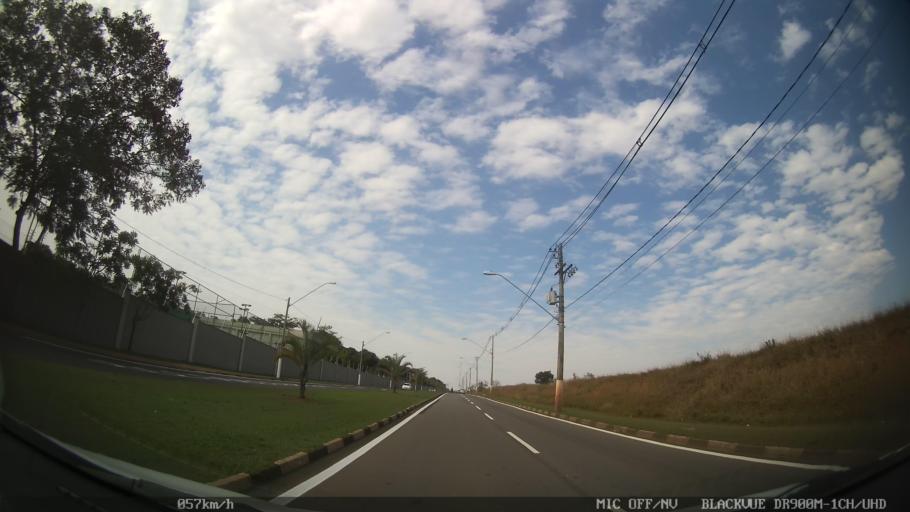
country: BR
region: Sao Paulo
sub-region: Paulinia
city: Paulinia
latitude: -22.7862
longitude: -47.1715
